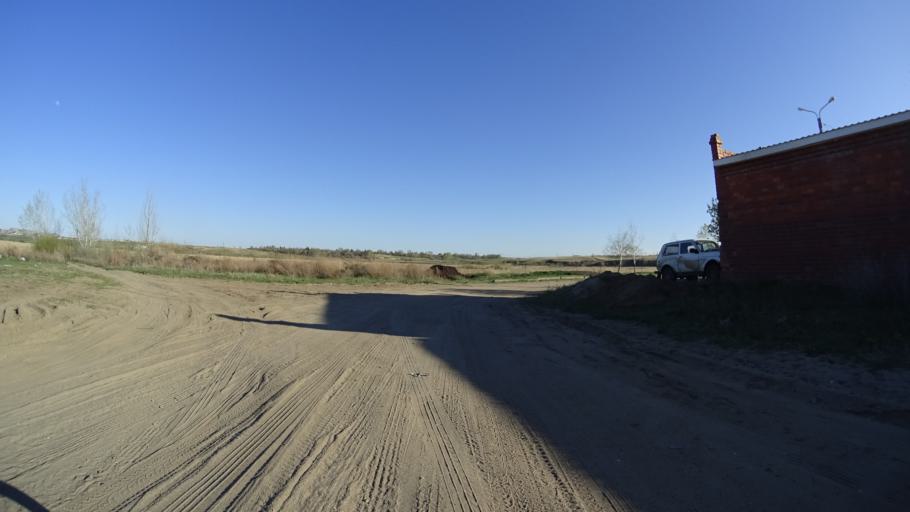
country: RU
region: Chelyabinsk
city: Troitsk
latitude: 54.0688
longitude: 61.5379
